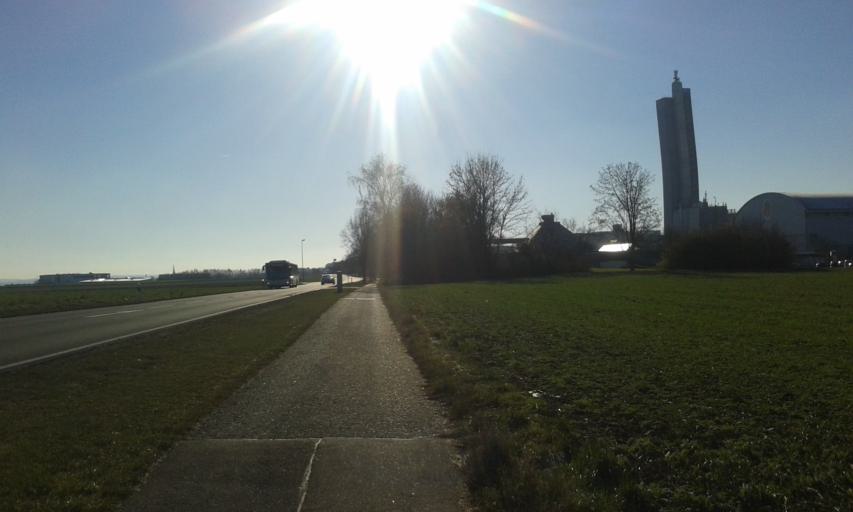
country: DE
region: Baden-Wuerttemberg
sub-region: Tuebingen Region
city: Ulm
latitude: 48.4367
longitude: 9.9863
